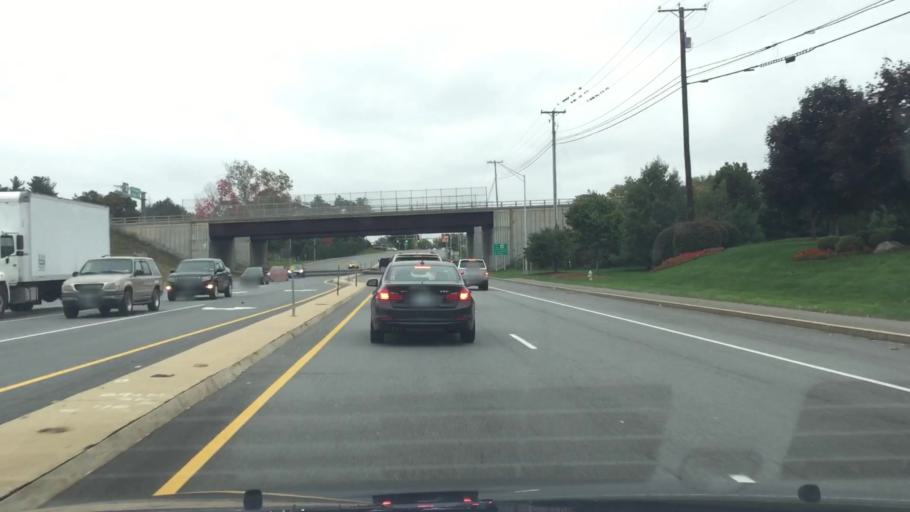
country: US
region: New Hampshire
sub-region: Hillsborough County
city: Hudson
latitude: 42.7239
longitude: -71.4449
